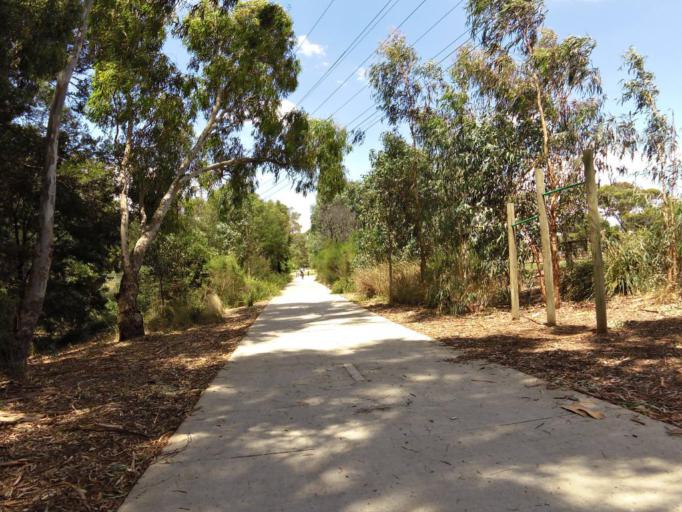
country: AU
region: Victoria
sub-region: Monash
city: Chadstone
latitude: -37.8900
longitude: 145.0932
